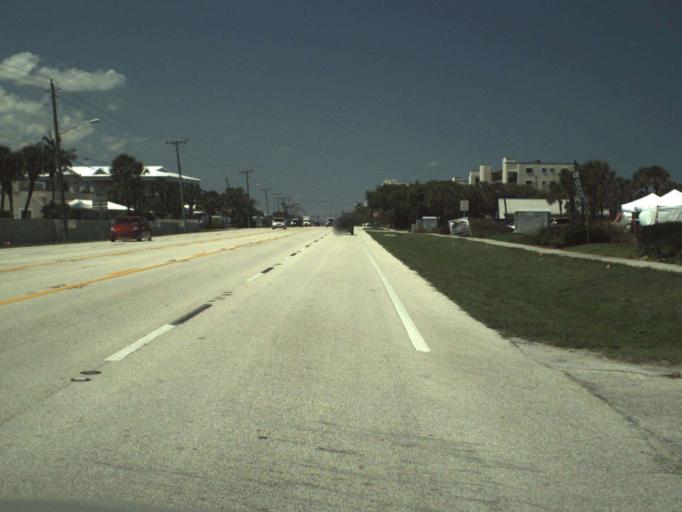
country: US
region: Florida
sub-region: Brevard County
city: Satellite Beach
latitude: 28.1678
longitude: -80.5882
